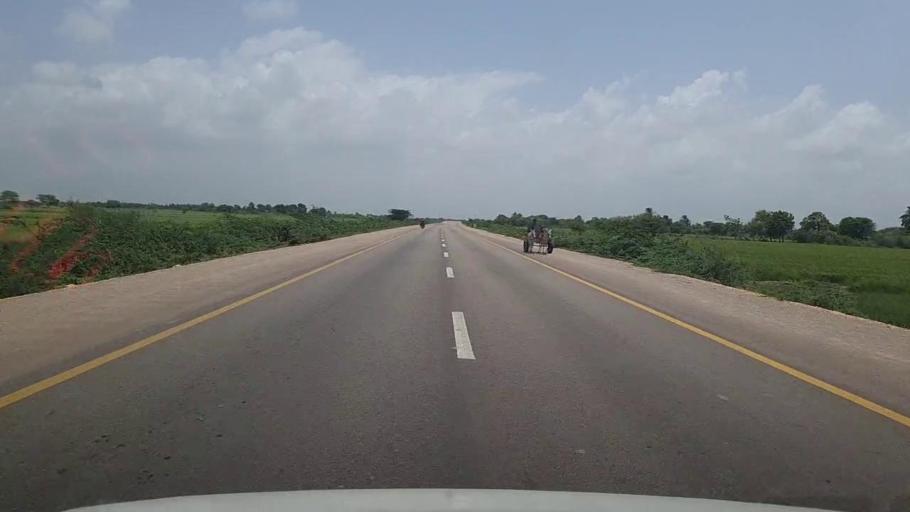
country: PK
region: Sindh
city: Thatta
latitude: 24.7672
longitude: 67.9446
